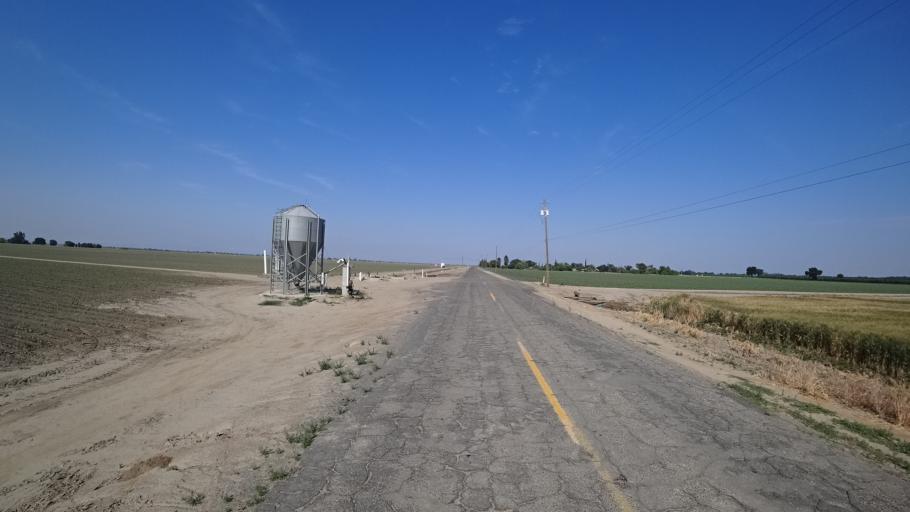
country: US
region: California
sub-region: Kings County
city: Lemoore
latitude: 36.3206
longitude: -119.8293
